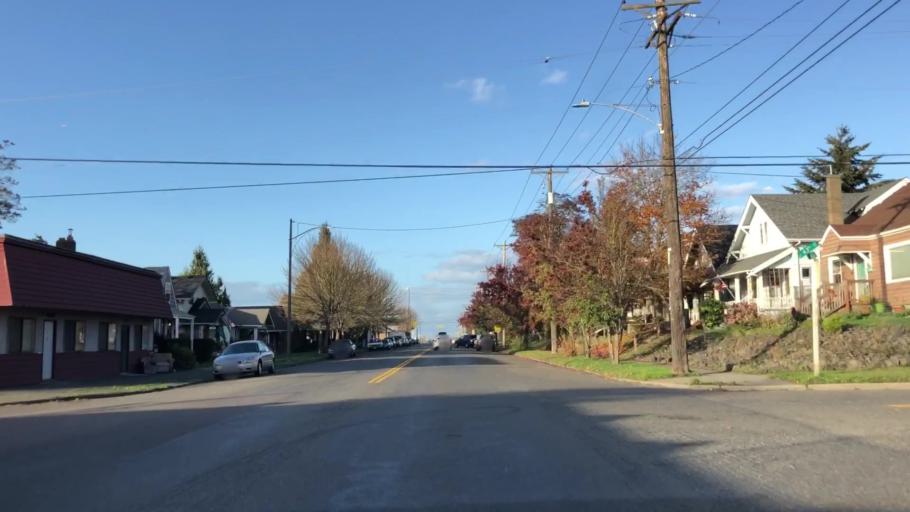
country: US
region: Washington
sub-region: Pierce County
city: Tacoma
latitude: 47.2184
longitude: -122.4508
